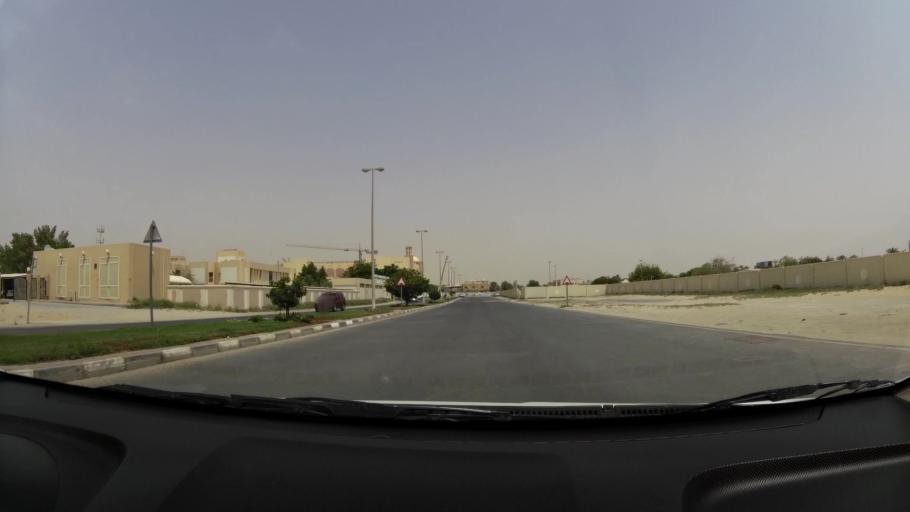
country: AE
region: Ash Shariqah
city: Sharjah
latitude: 25.3494
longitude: 55.4061
